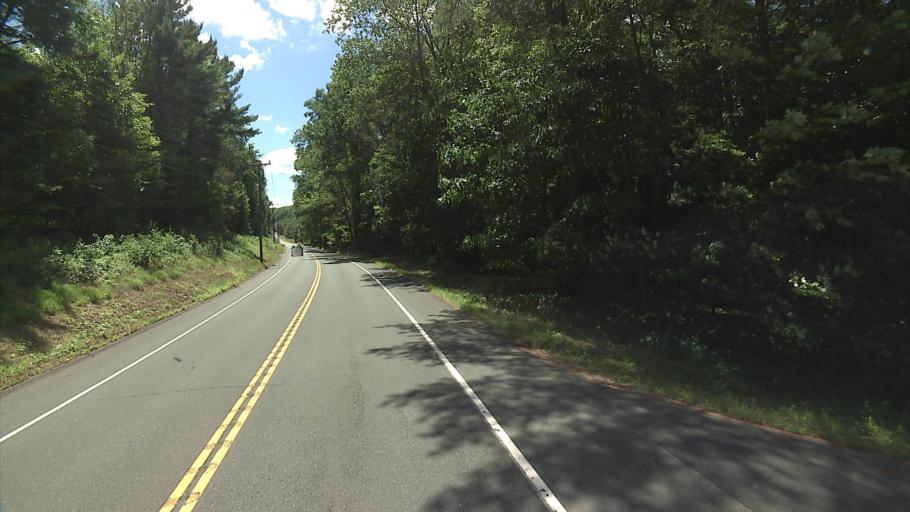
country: US
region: Connecticut
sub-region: Litchfield County
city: New Hartford Center
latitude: 41.8349
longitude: -73.0174
